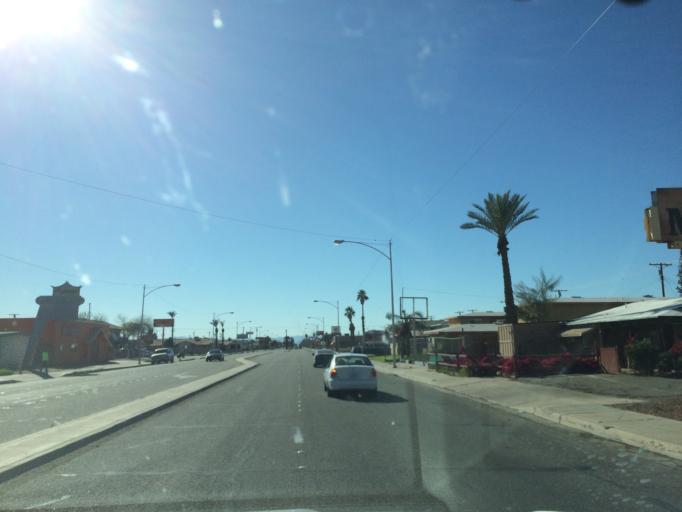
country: US
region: California
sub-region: Imperial County
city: El Centro
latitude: 32.7966
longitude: -115.5618
